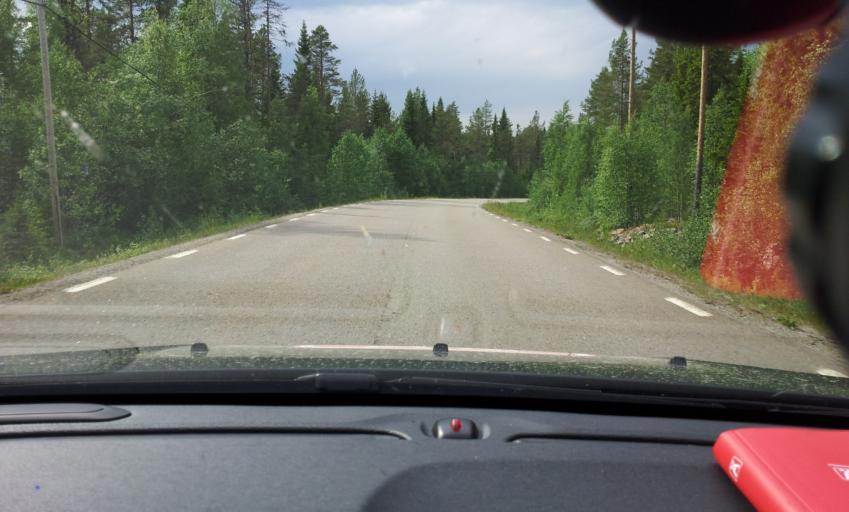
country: SE
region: Jaemtland
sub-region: Bergs Kommun
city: Hoverberg
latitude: 62.6629
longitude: 14.7658
